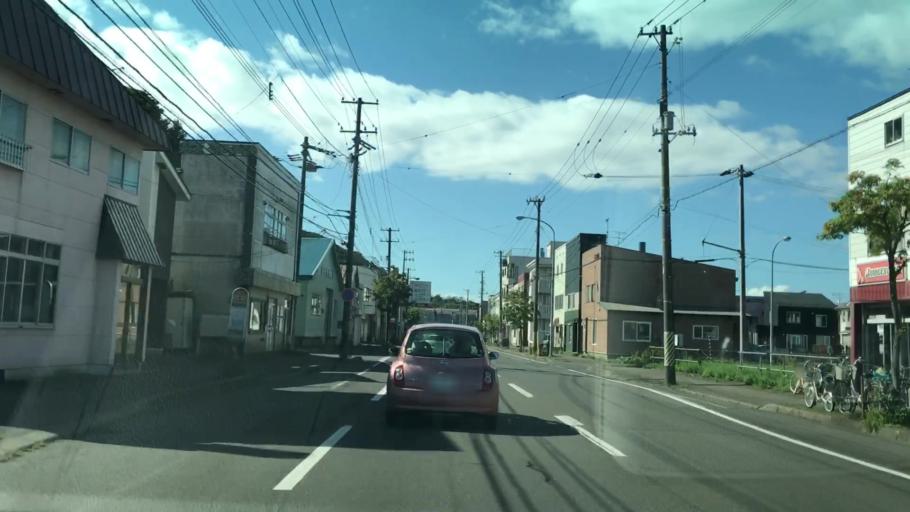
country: JP
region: Hokkaido
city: Muroran
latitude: 42.3339
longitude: 140.9614
